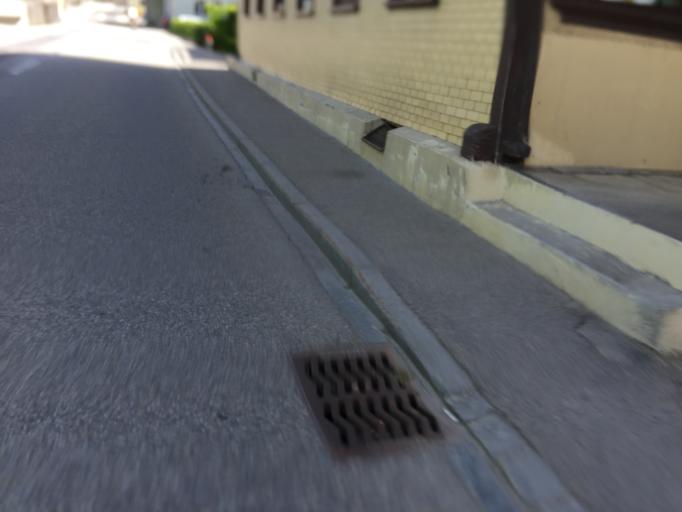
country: CH
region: Bern
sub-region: Emmental District
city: Signau
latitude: 46.9177
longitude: 7.7218
